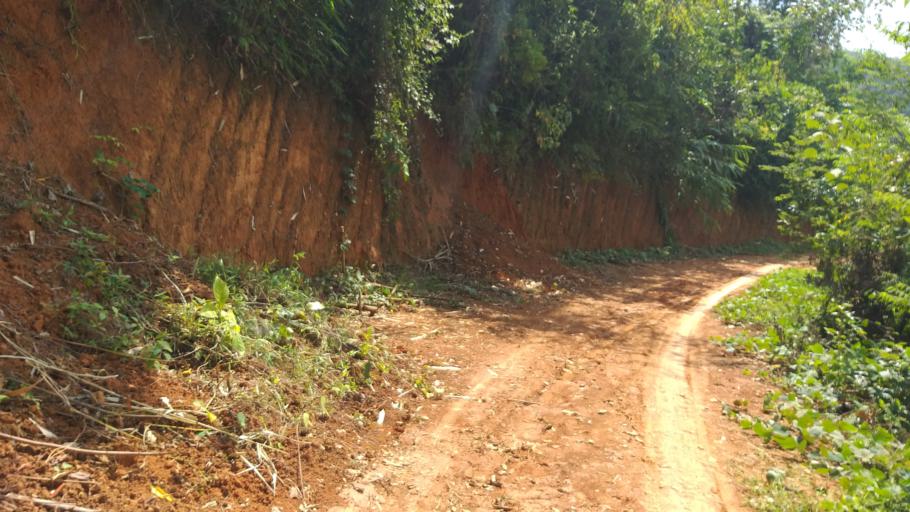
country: LA
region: Phongsali
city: Khoa
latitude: 21.2754
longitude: 102.5241
